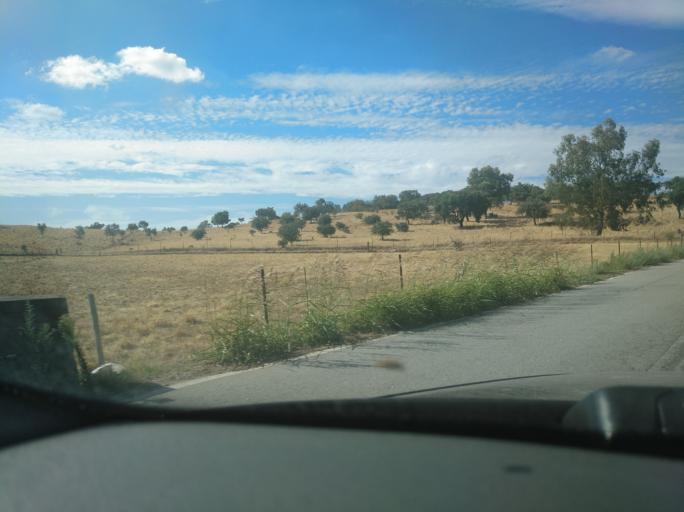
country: ES
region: Extremadura
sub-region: Provincia de Badajoz
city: La Codosera
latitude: 39.1634
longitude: -7.1862
